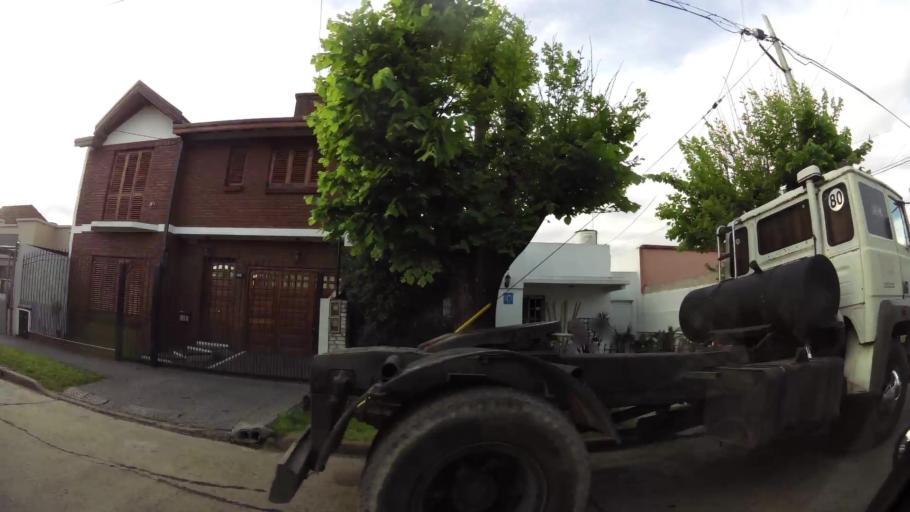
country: AR
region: Buenos Aires
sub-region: Partido de Quilmes
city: Quilmes
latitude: -34.7363
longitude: -58.2658
